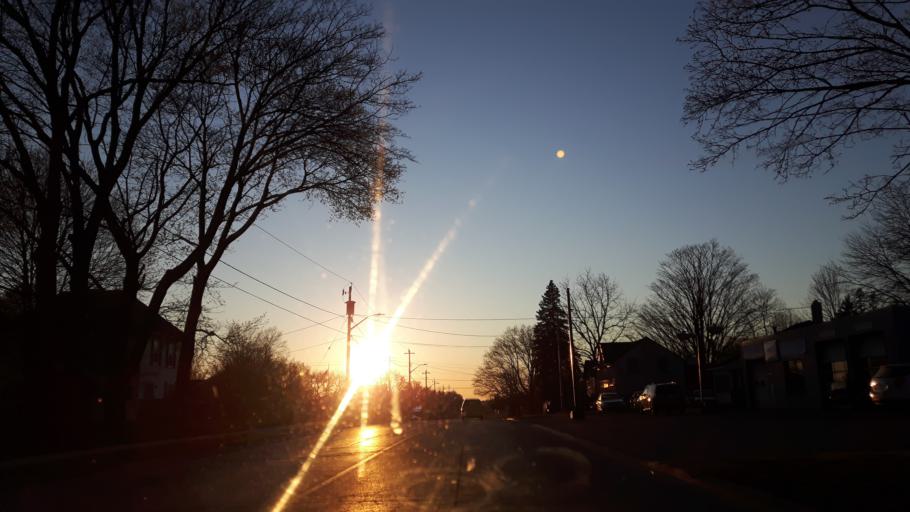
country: CA
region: Ontario
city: Bluewater
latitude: 43.6201
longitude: -81.5464
